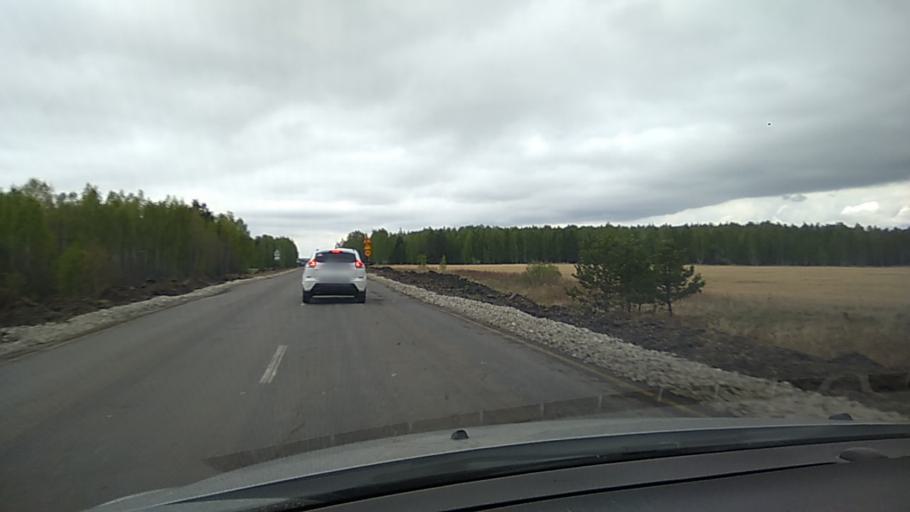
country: RU
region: Kurgan
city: Shadrinsk
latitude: 56.1506
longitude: 63.4469
